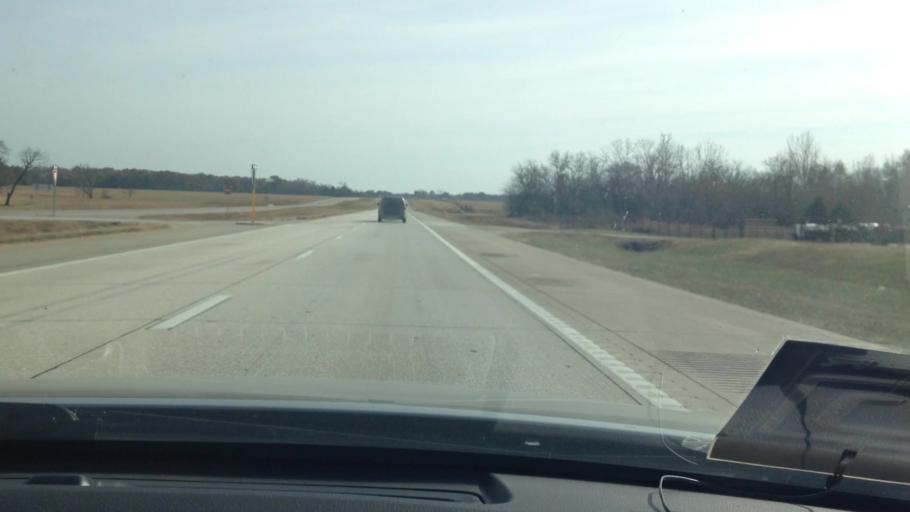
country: US
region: Missouri
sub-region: Henry County
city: Clinton
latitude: 38.4126
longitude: -93.8564
